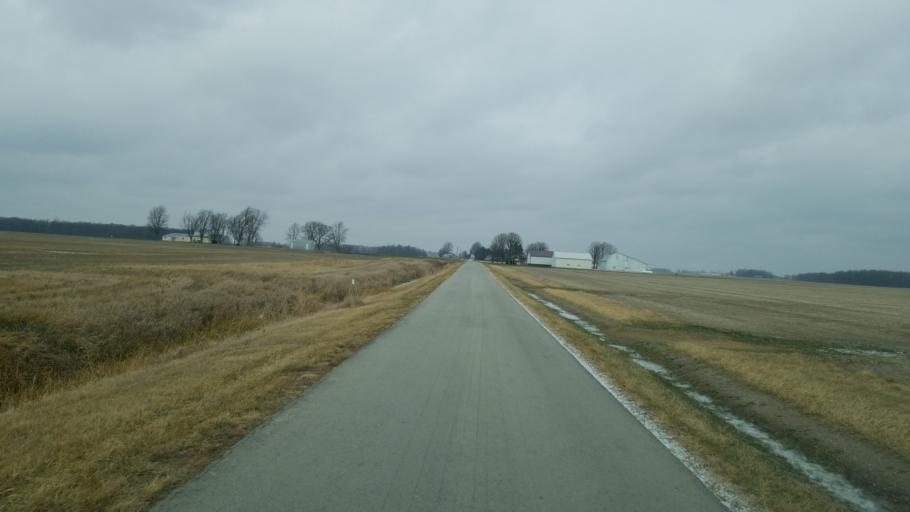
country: US
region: Ohio
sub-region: Hardin County
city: Forest
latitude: 40.7557
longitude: -83.4777
